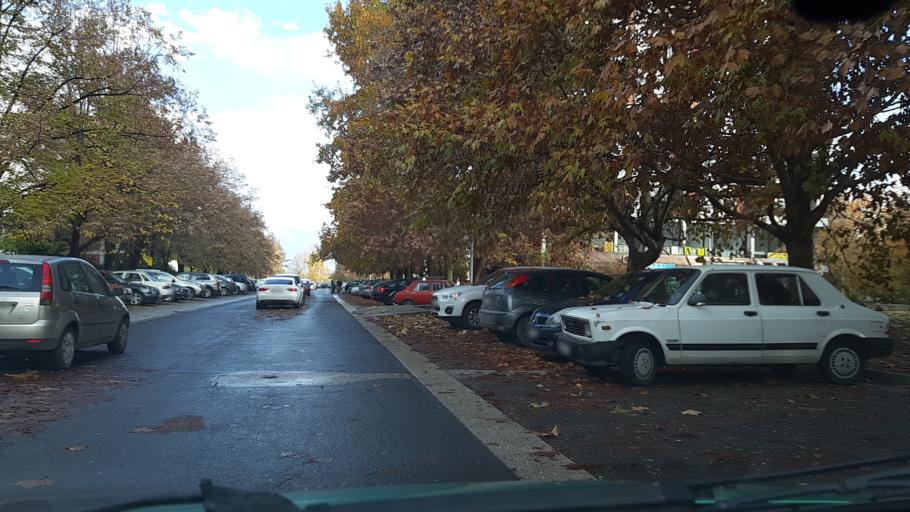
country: MK
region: Kisela Voda
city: Usje
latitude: 41.9893
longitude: 21.4678
